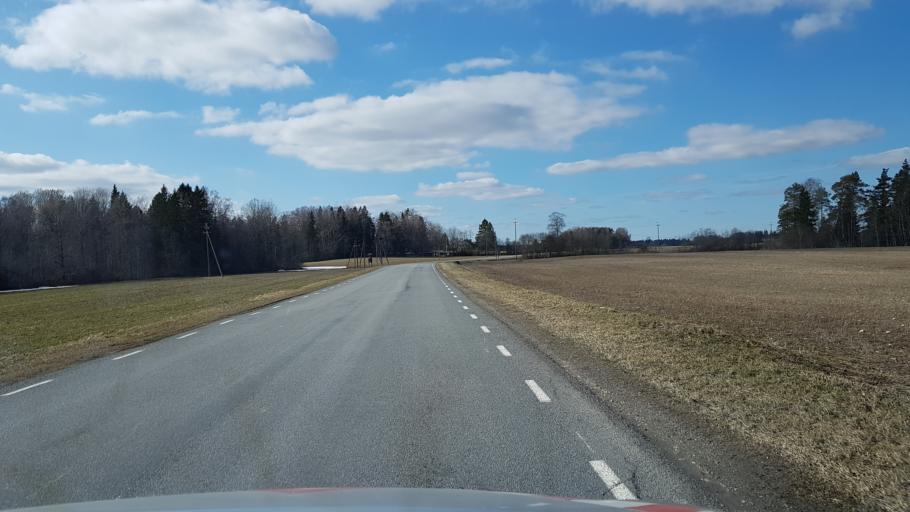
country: EE
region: Laeaene-Virumaa
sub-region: Tamsalu vald
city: Tamsalu
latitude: 59.1679
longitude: 26.0664
